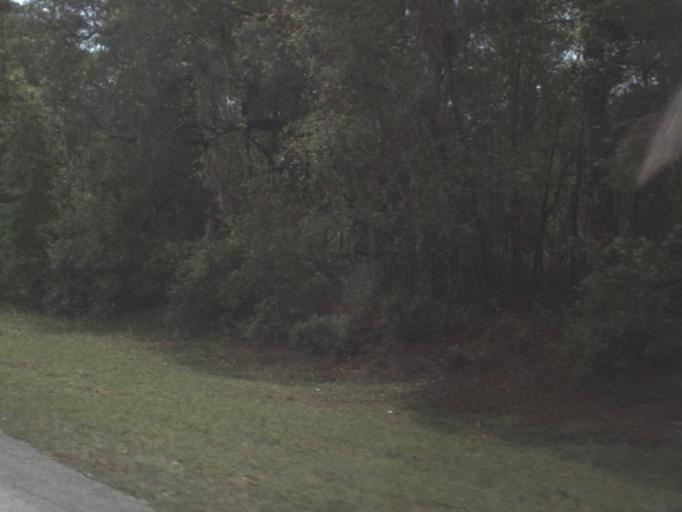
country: US
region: Florida
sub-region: Putnam County
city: Crescent City
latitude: 29.3410
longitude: -81.7320
